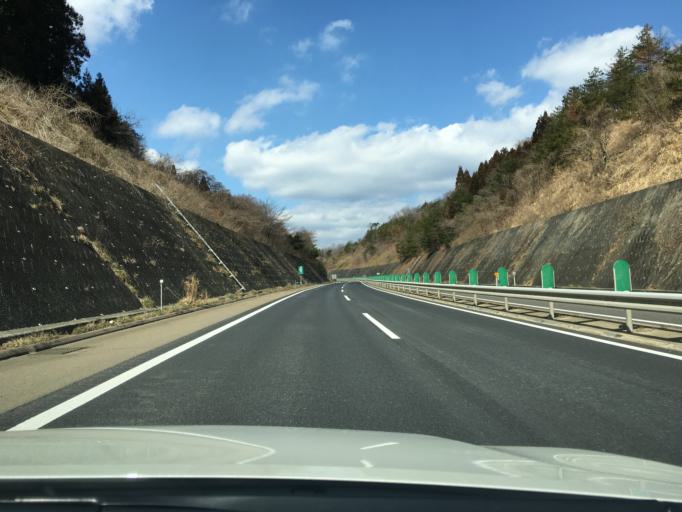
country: JP
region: Miyagi
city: Okawara
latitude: 38.1507
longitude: 140.6982
